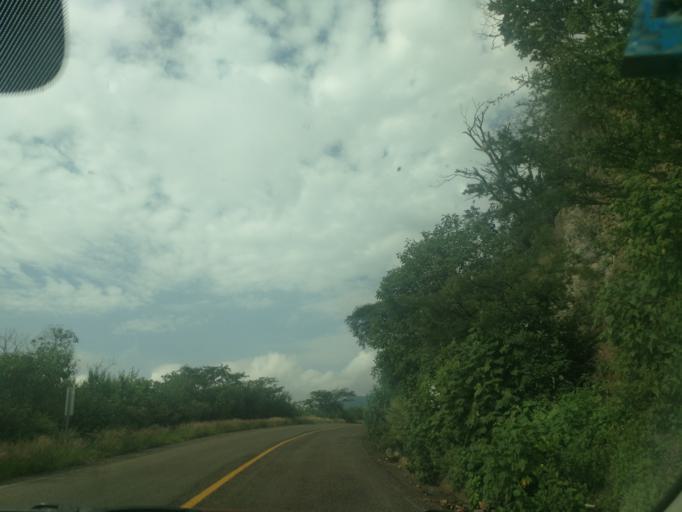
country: MX
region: Jalisco
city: El Salto
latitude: 20.3630
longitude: -104.5841
